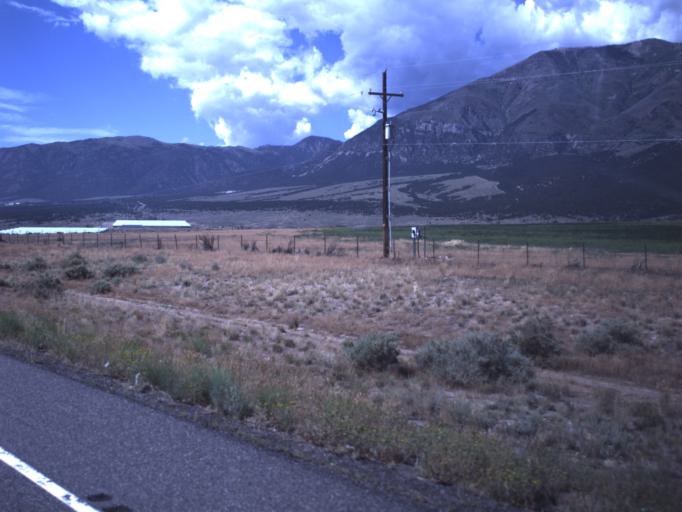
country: US
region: Utah
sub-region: Piute County
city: Junction
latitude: 38.4192
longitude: -112.2315
